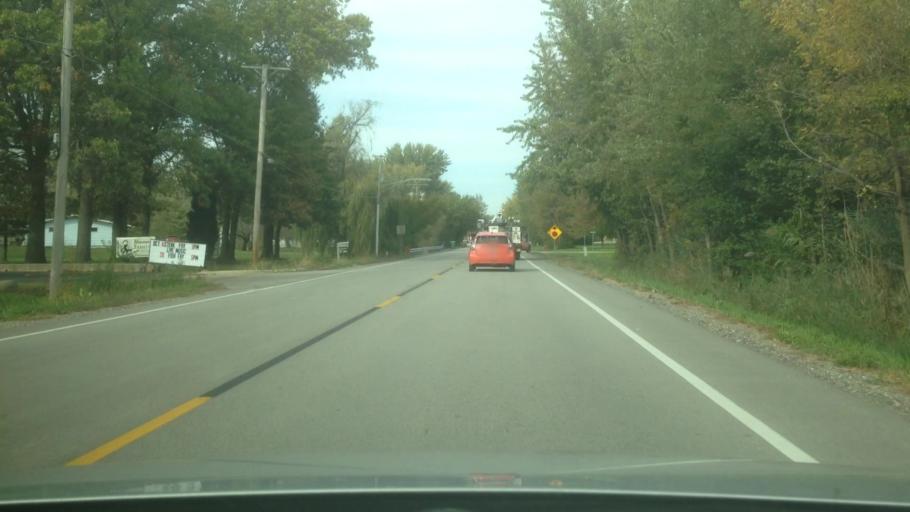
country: US
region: Illinois
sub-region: Will County
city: Wilmington
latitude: 41.3016
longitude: -88.1588
